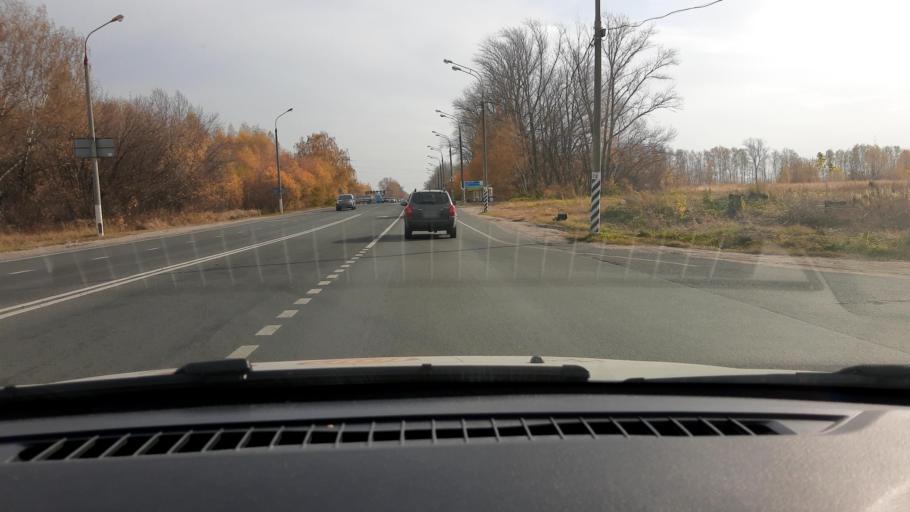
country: RU
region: Nizjnij Novgorod
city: Kstovo
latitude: 56.1425
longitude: 44.2246
